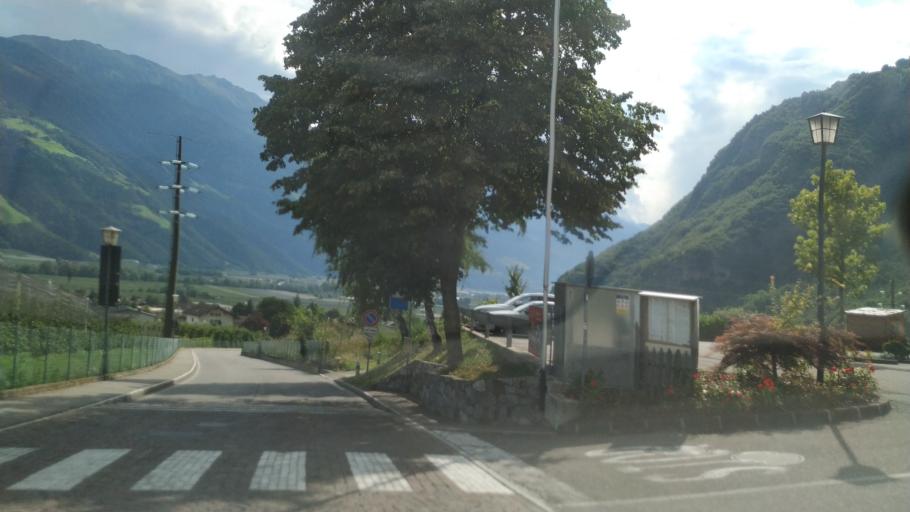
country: IT
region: Trentino-Alto Adige
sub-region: Bolzano
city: Rabla
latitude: 46.6772
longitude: 11.0619
